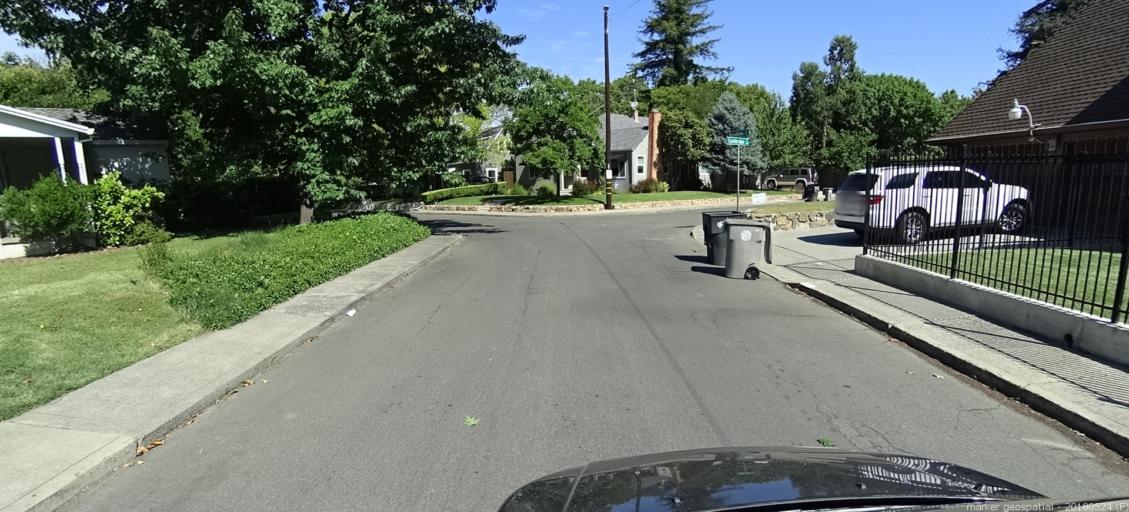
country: US
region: California
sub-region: Sacramento County
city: Sacramento
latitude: 38.6049
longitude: -121.4498
